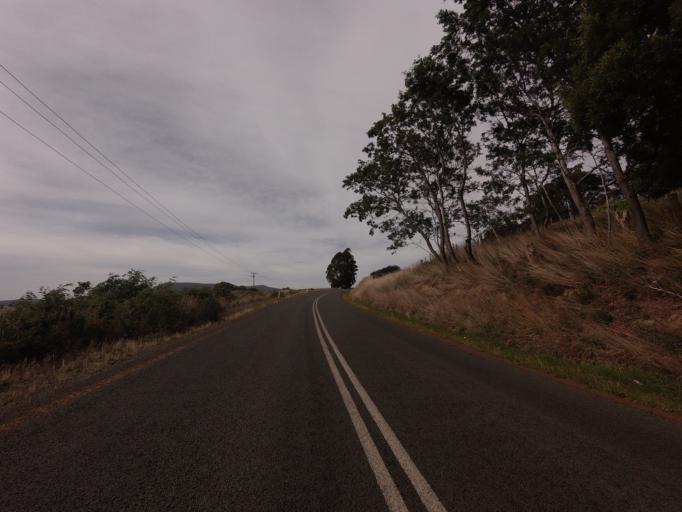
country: AU
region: Tasmania
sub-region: Sorell
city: Sorell
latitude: -42.4194
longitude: 147.4648
